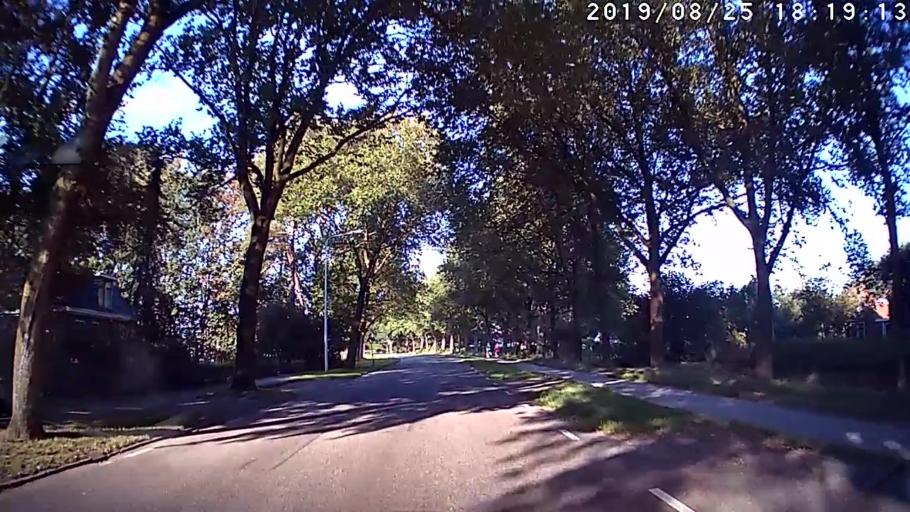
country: NL
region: Friesland
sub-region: Gemeente Gaasterlan-Sleat
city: Balk
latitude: 52.8727
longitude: 5.6008
